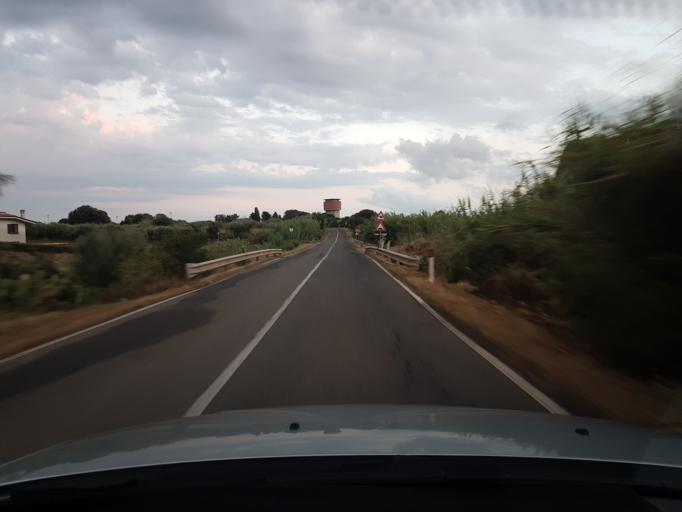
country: IT
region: Sardinia
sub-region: Provincia di Oristano
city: Tramatza
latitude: 40.0098
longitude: 8.6461
